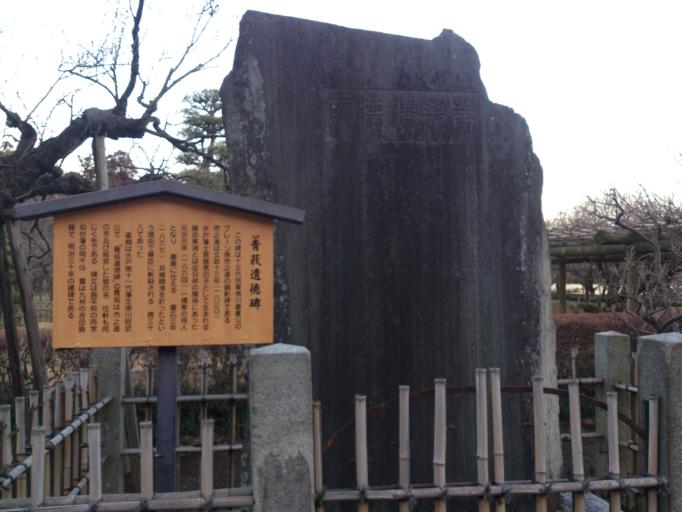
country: JP
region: Ibaraki
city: Mito-shi
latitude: 36.3746
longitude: 140.4535
